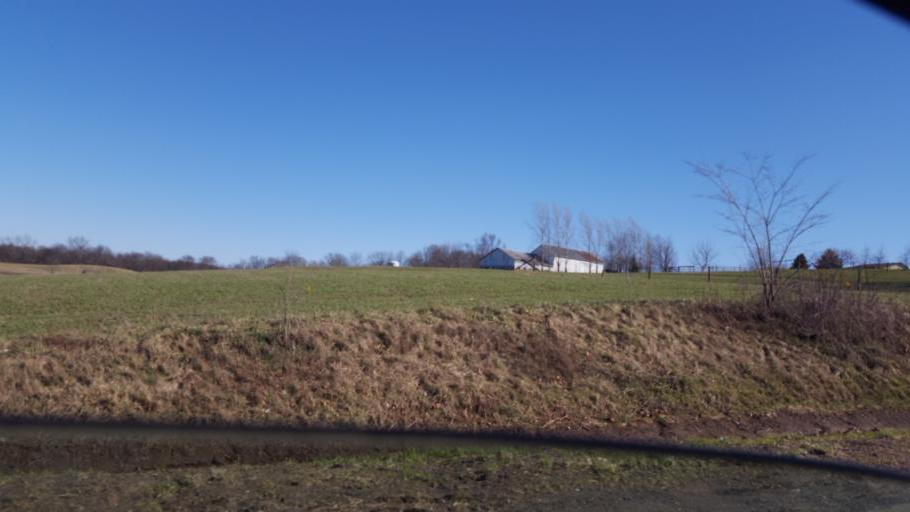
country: US
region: Ohio
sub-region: Wayne County
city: Dalton
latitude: 40.7188
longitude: -81.6958
